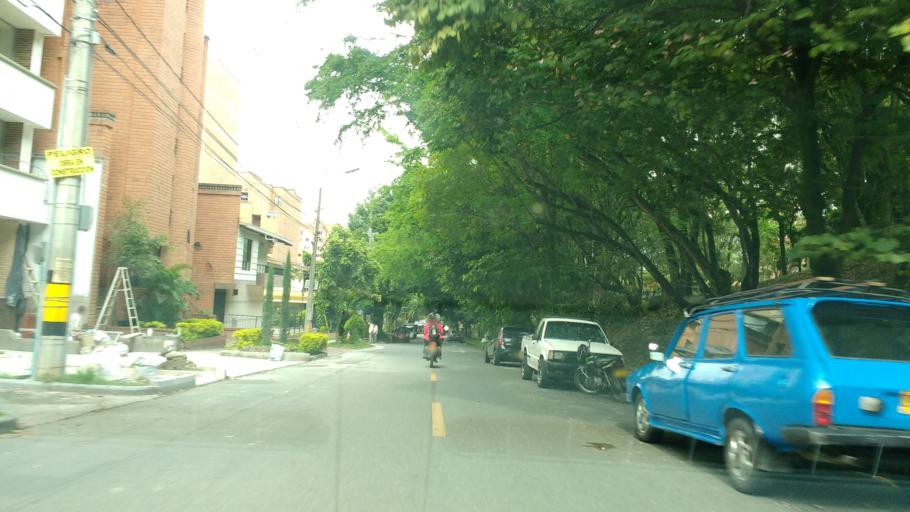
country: CO
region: Antioquia
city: Medellin
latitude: 6.2376
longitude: -75.6051
